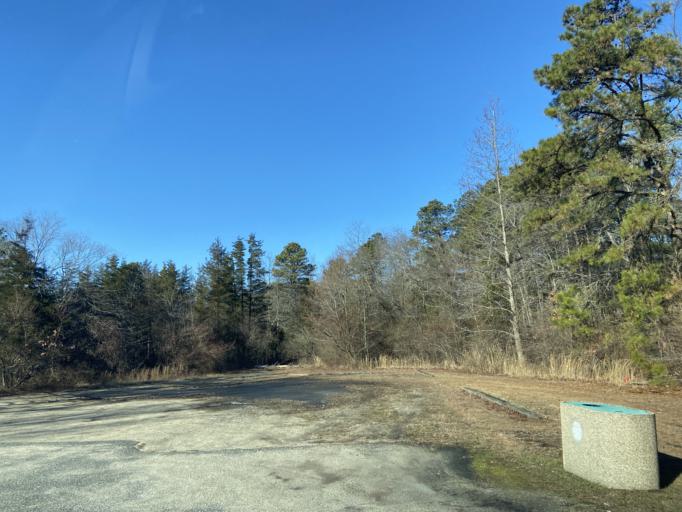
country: US
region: New Jersey
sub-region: Cumberland County
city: Vineland
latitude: 39.4967
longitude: -75.0757
